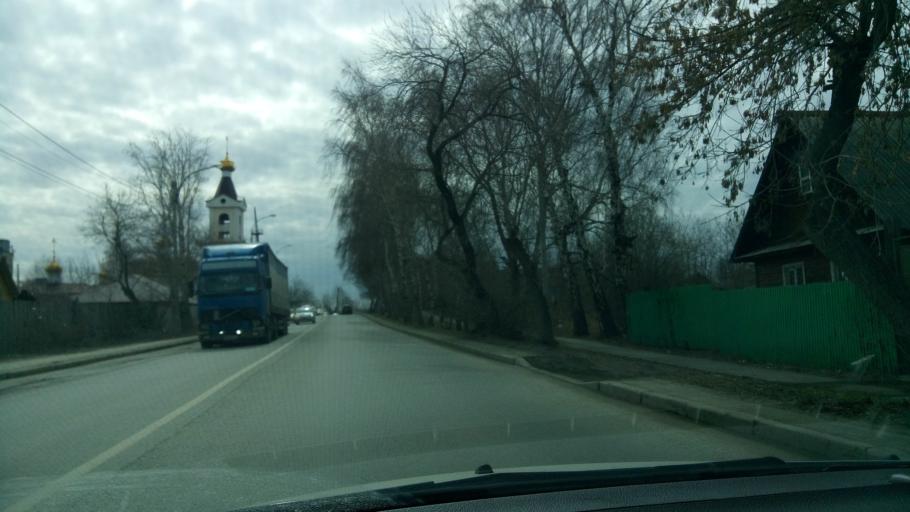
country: RU
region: Sverdlovsk
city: Yekaterinburg
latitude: 56.8773
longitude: 60.6919
